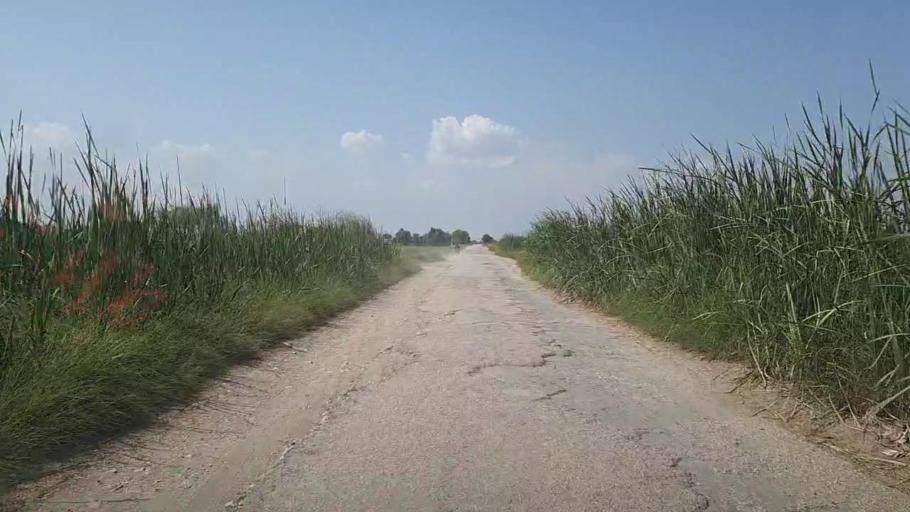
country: PK
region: Sindh
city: Khairpur
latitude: 28.0901
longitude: 69.6313
